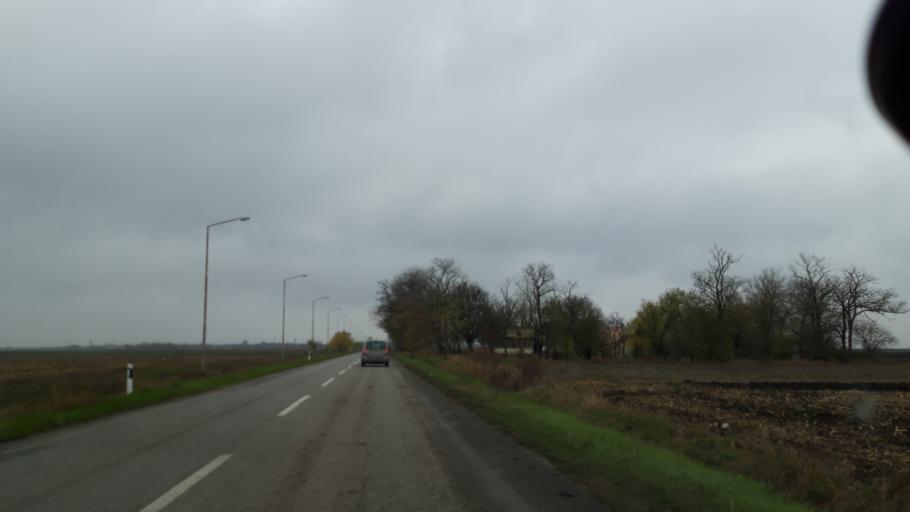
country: RS
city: Backo Gradiste
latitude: 45.4980
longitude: 19.9482
